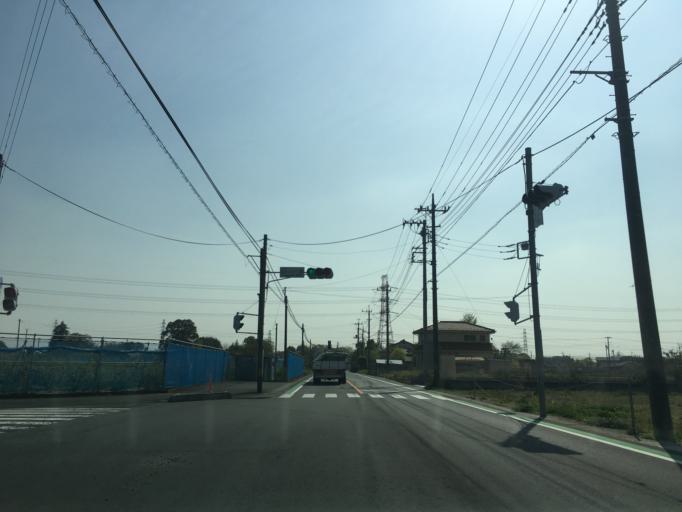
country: JP
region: Saitama
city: Sugito
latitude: 36.0081
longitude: 139.7129
